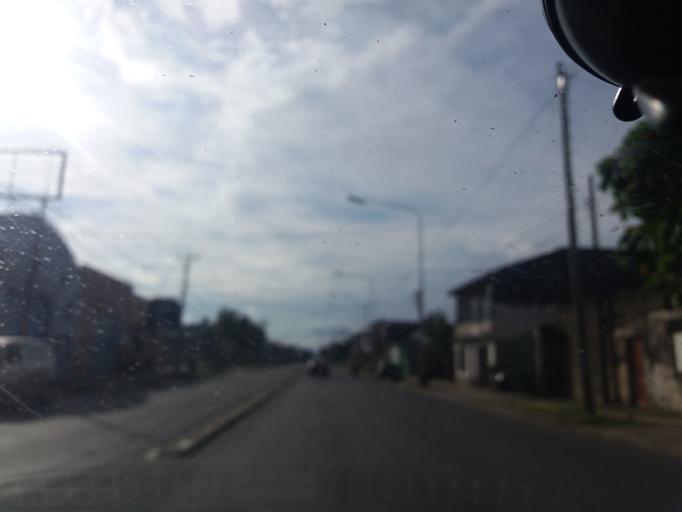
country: AR
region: Corrientes
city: Corrientes
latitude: -27.4891
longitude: -58.8210
